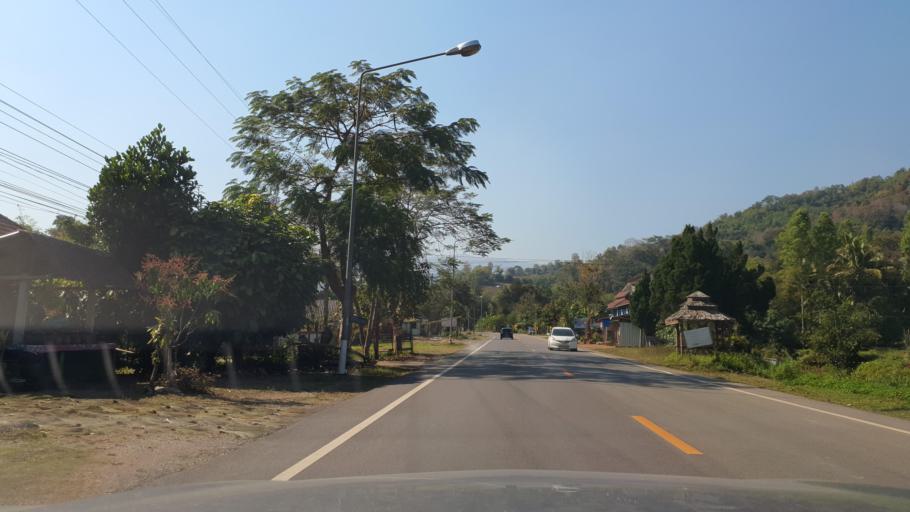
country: TH
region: Chiang Rai
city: Mae Lao
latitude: 19.8387
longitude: 99.6797
